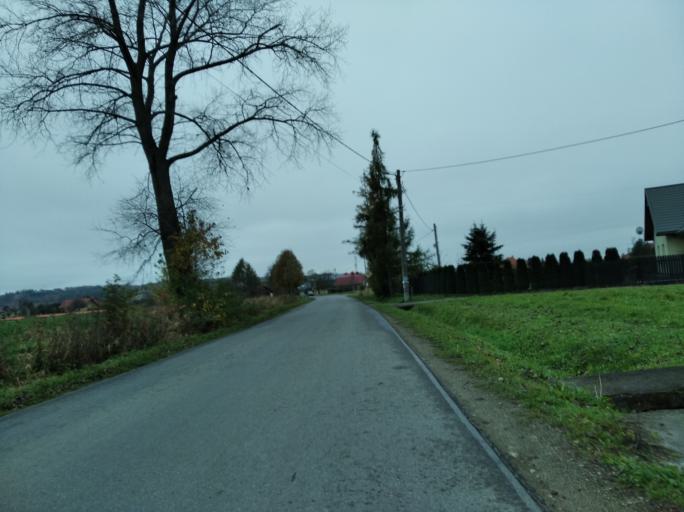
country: PL
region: Subcarpathian Voivodeship
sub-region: Powiat krosnienski
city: Odrzykon
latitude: 49.7251
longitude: 21.7633
